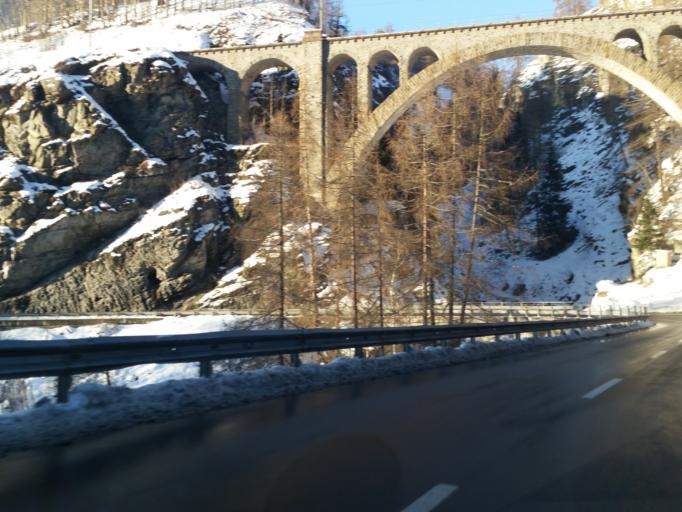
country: CH
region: Grisons
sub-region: Inn District
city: Zernez
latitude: 46.7699
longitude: 10.1422
